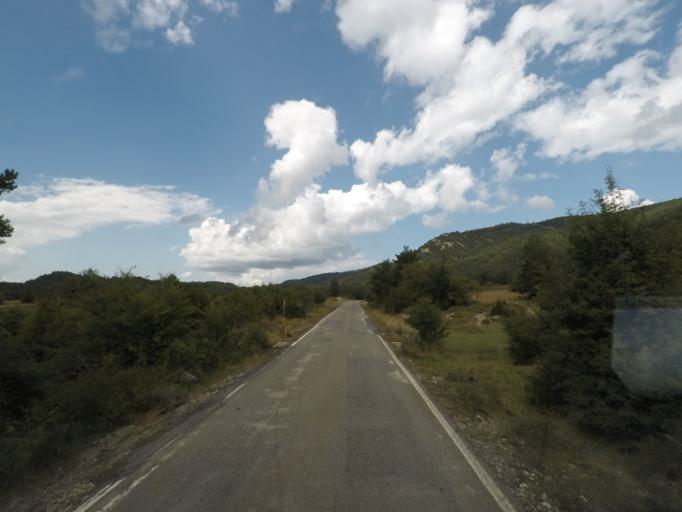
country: ES
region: Aragon
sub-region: Provincia de Huesca
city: Fiscal
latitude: 42.4014
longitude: -0.0542
